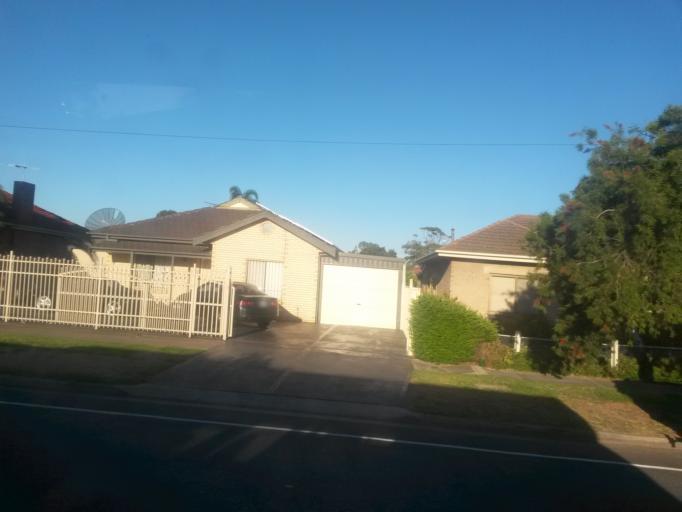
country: AU
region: South Australia
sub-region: Port Adelaide Enfield
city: Alberton
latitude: -34.8604
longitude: 138.5292
